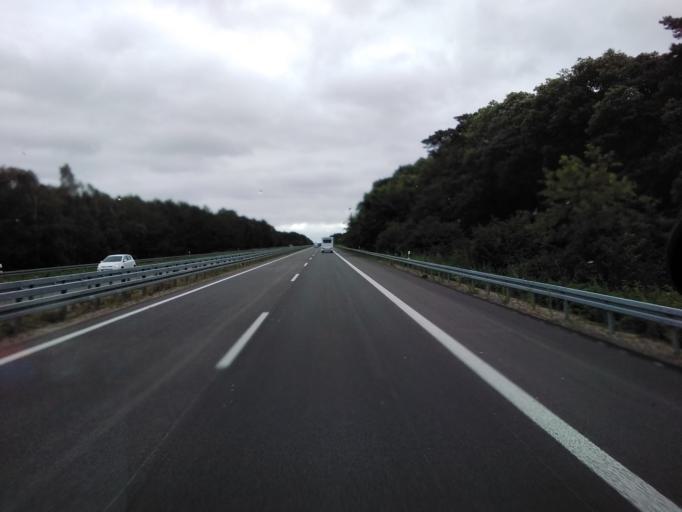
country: DE
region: North Rhine-Westphalia
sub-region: Regierungsbezirk Dusseldorf
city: Issum
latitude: 51.5763
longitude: 6.4219
